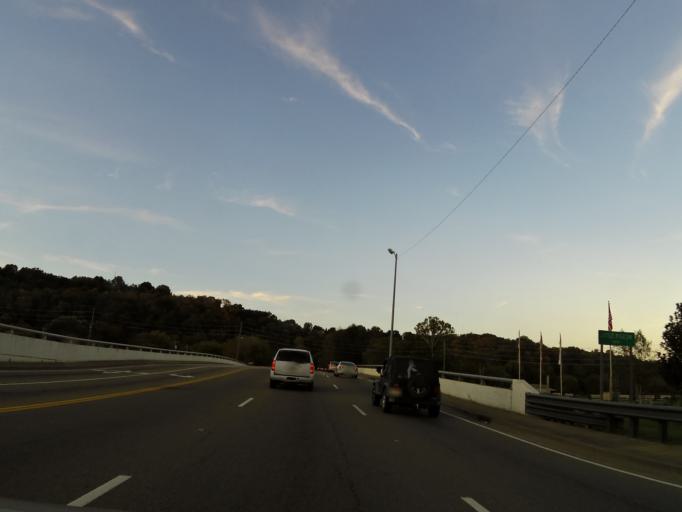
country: US
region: Tennessee
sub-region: Sevier County
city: Sevierville
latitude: 35.8690
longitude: -83.5627
